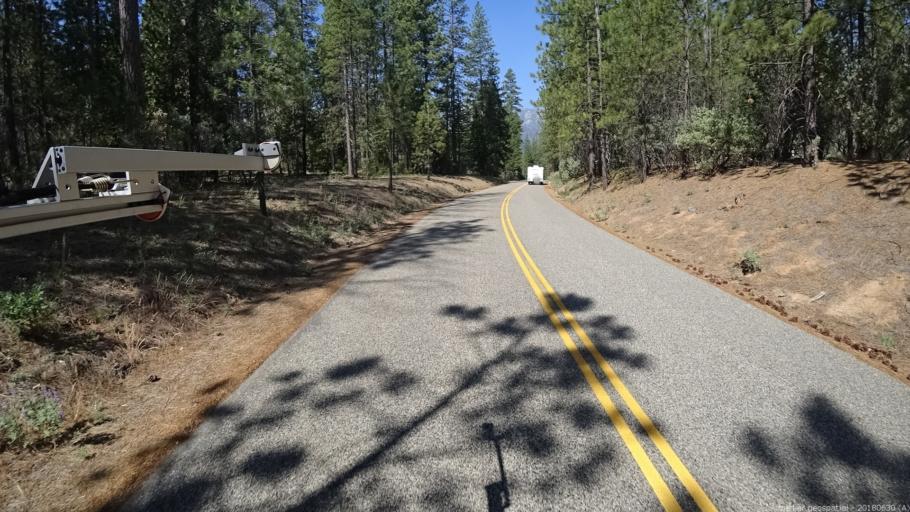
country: US
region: California
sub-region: Madera County
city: Oakhurst
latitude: 37.3765
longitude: -119.3766
